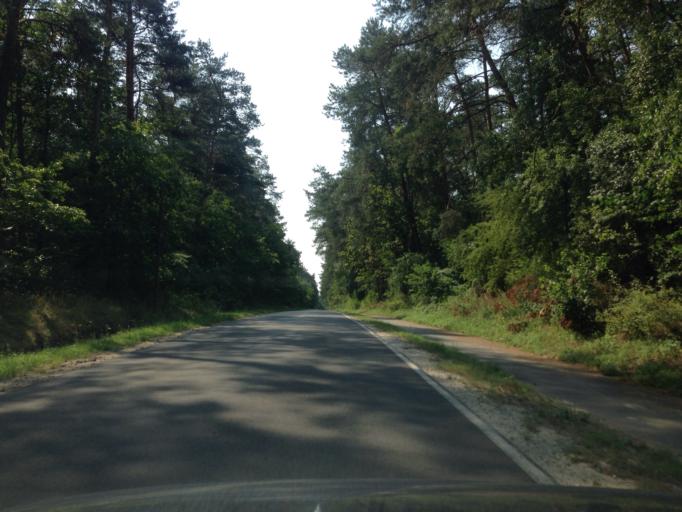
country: PL
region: Kujawsko-Pomorskie
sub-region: Powiat golubsko-dobrzynski
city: Golub-Dobrzyn
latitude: 53.0894
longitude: 19.0362
